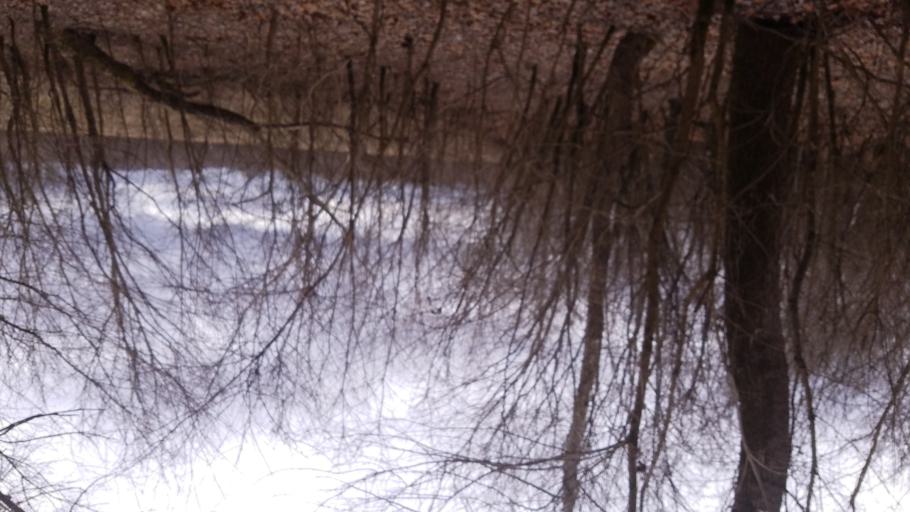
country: US
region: Ohio
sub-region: Muskingum County
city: Frazeysburg
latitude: 40.0462
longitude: -82.1372
